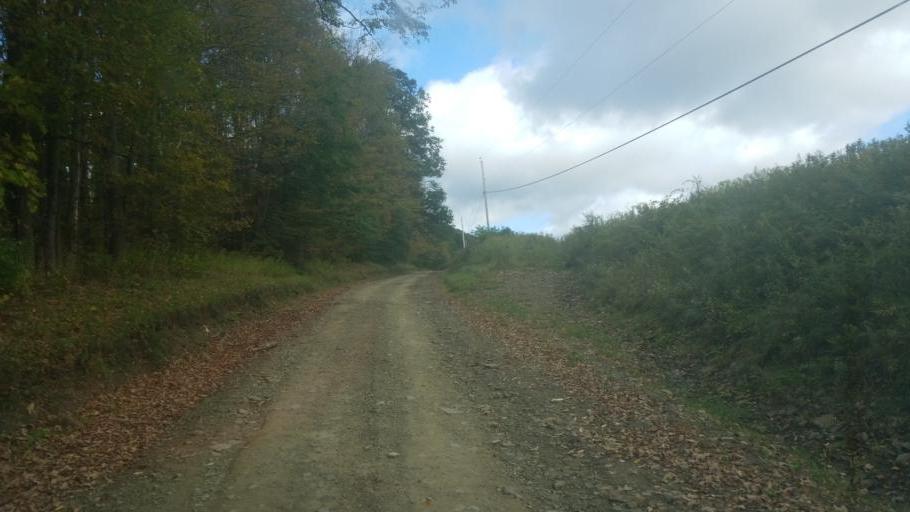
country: US
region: New York
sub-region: Allegany County
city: Cuba
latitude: 42.1342
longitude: -78.3016
